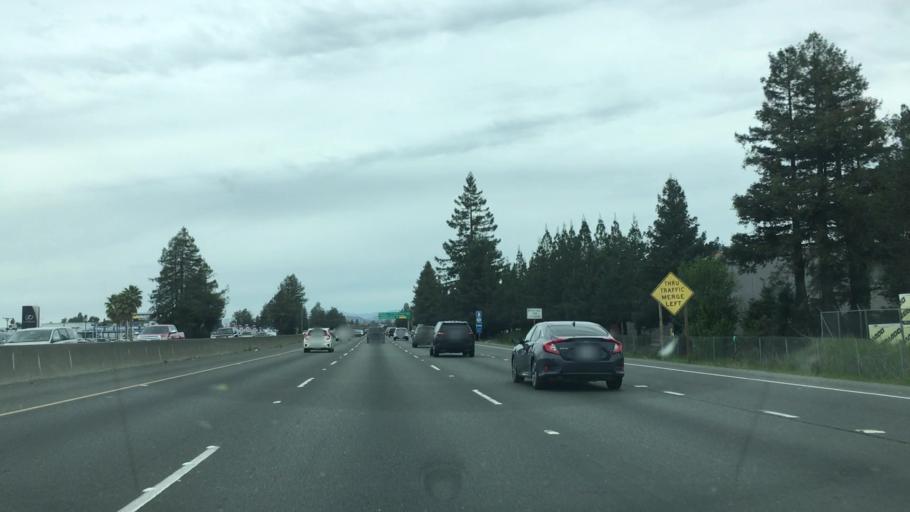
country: US
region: California
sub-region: Sonoma County
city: Roseland
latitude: 38.4075
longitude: -122.7160
